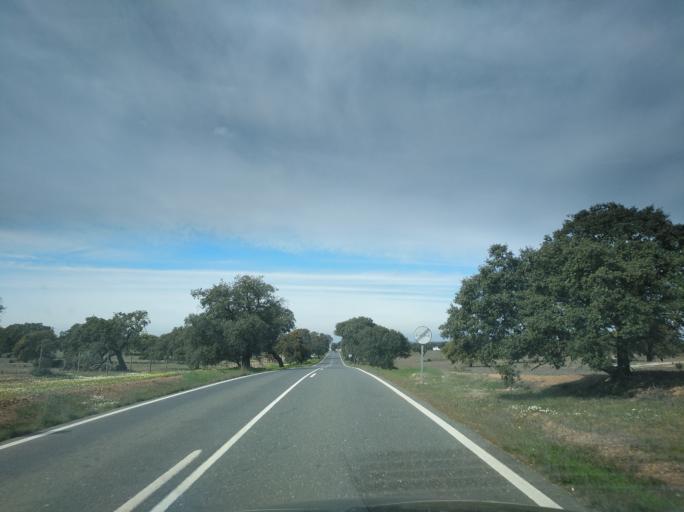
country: PT
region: Beja
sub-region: Mertola
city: Mertola
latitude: 37.7564
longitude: -7.8098
